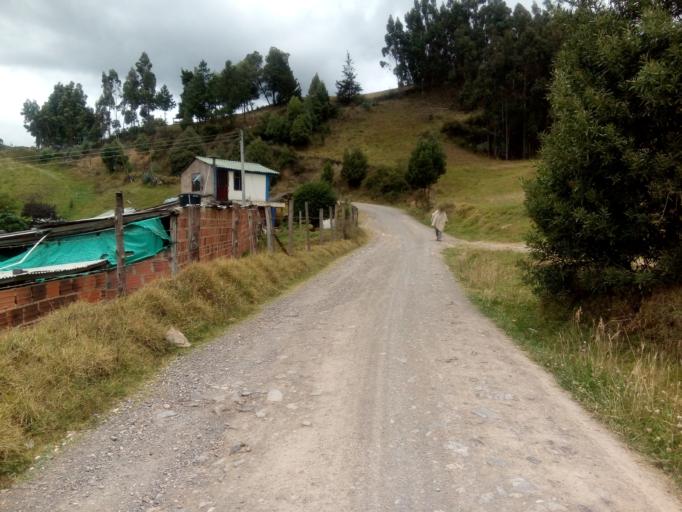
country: CO
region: Boyaca
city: Gameza
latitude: 5.8157
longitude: -72.8029
